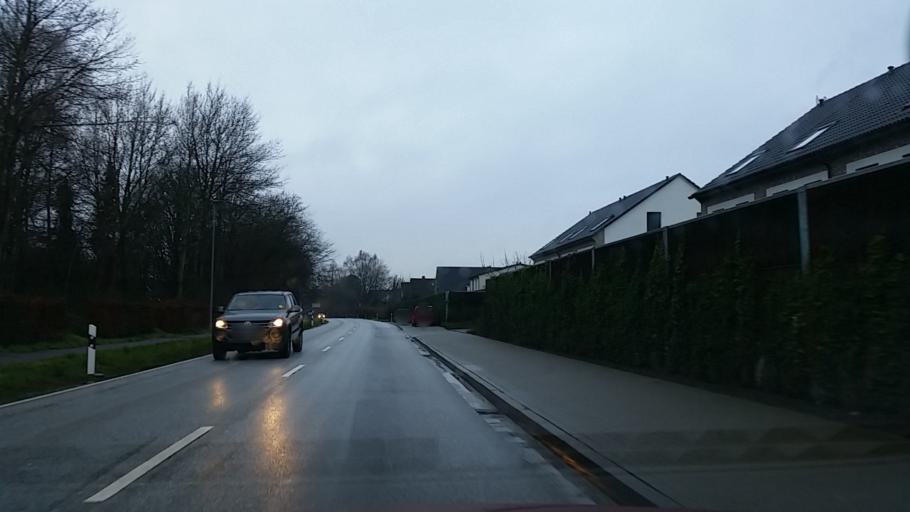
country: DE
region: Schleswig-Holstein
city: Wedel
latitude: 53.5891
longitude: 9.6895
